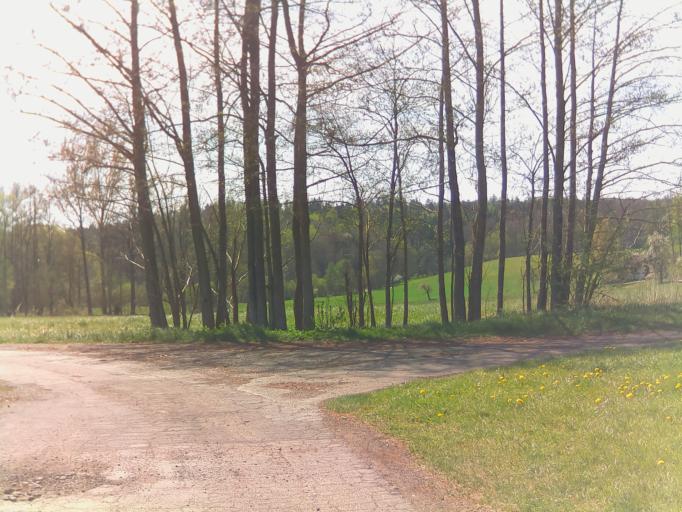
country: DE
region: Thuringia
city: Veilsdorf
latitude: 50.3019
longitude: 10.7965
